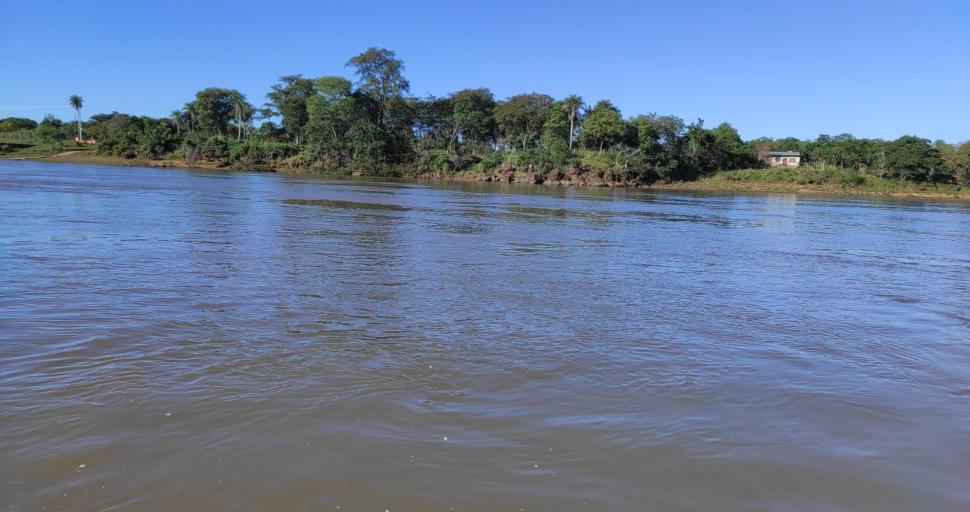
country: AR
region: Corrientes
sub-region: Departamento de Itati
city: Itati
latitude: -27.2634
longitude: -58.2656
